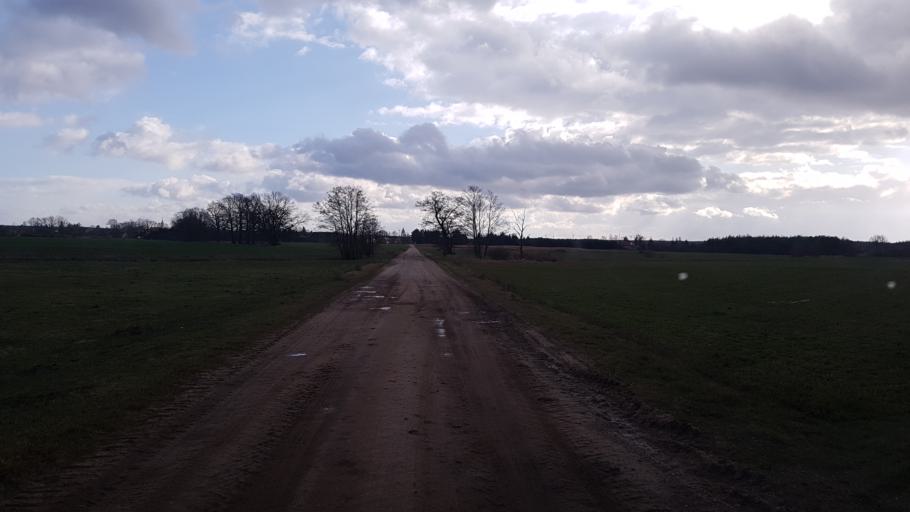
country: DE
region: Brandenburg
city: Sallgast
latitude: 51.6170
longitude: 13.8558
